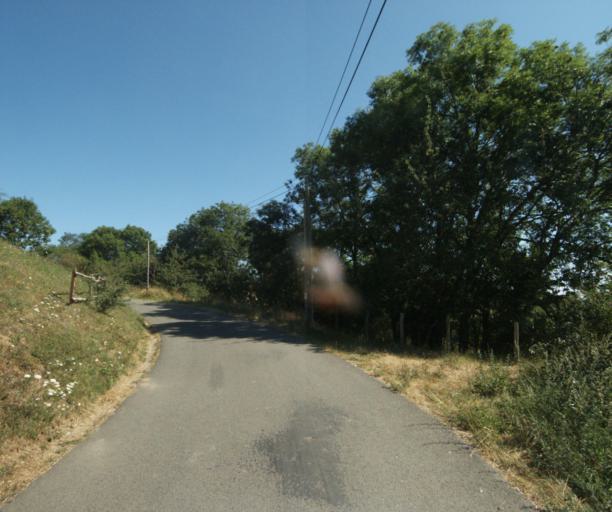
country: FR
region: Rhone-Alpes
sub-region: Departement du Rhone
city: Saint-Romain-de-Popey
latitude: 45.8131
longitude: 4.5070
